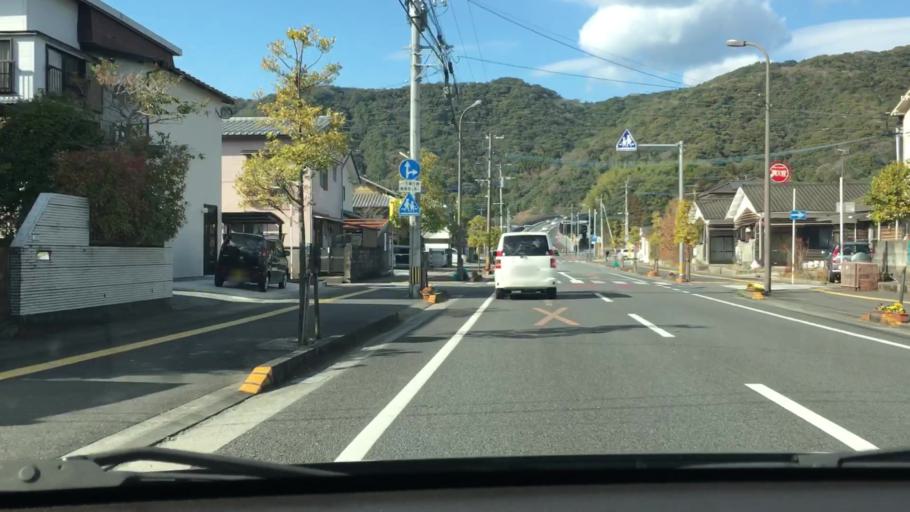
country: JP
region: Oita
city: Saiki
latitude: 32.9630
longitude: 131.8975
